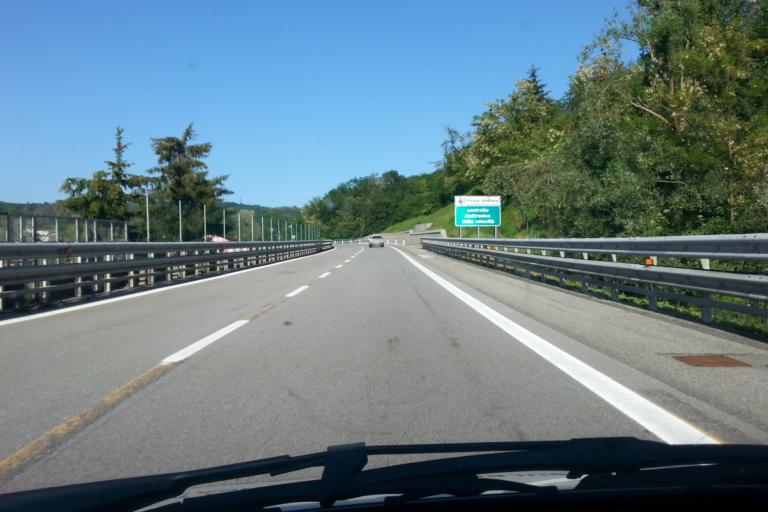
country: IT
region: Liguria
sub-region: Provincia di Savona
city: Carcare
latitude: 44.3525
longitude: 8.2844
